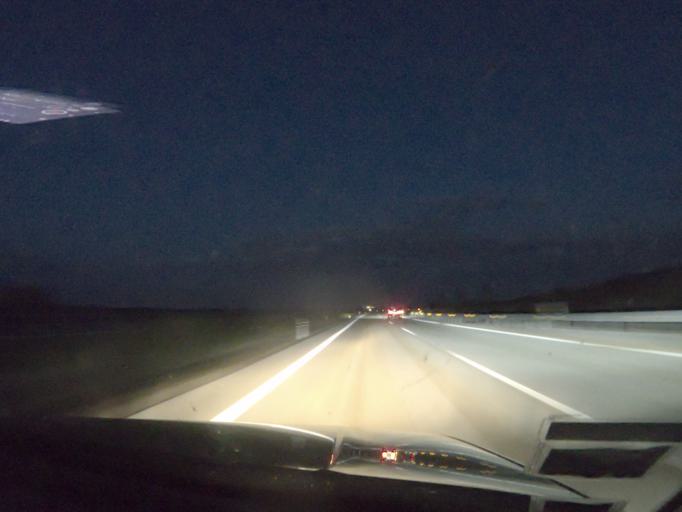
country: ES
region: Castille and Leon
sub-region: Provincia de Leon
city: Brazuelo
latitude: 42.5268
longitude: -6.1334
